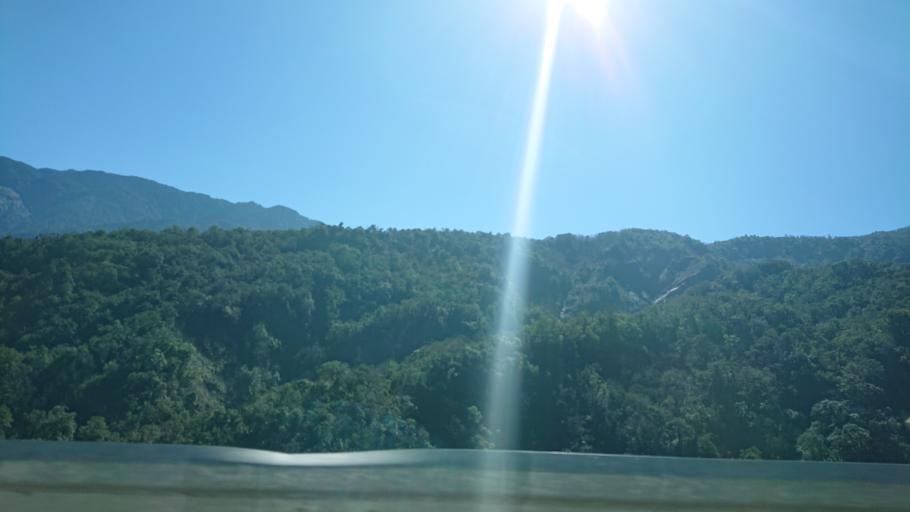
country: TW
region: Taiwan
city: Daxi
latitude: 24.4144
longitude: 121.3665
